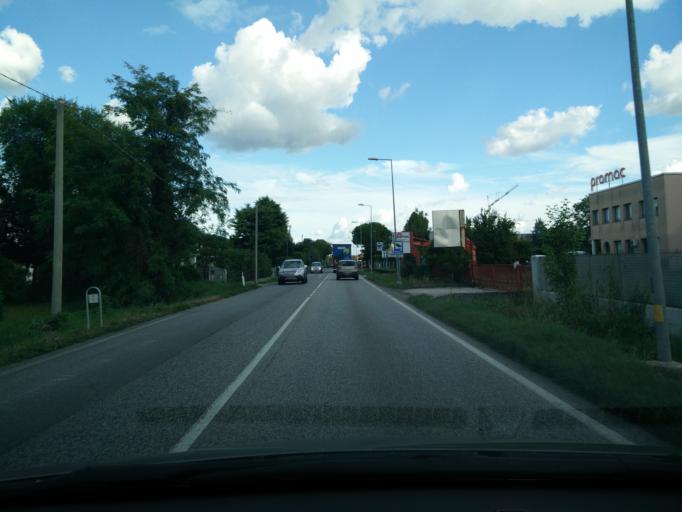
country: IT
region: Veneto
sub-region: Provincia di Treviso
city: Lancenigo-Villorba
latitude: 45.7333
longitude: 12.2437
